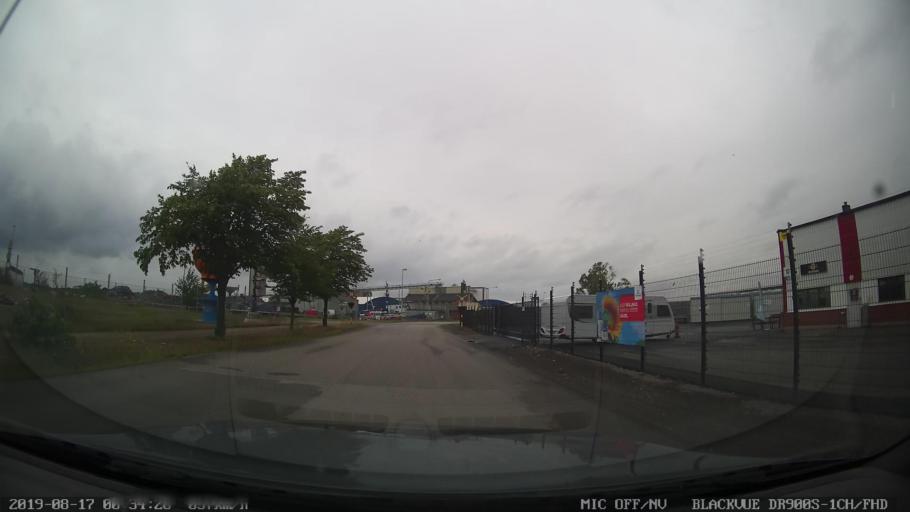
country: SE
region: Skane
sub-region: Landskrona
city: Landskrona
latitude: 55.8598
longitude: 12.8384
